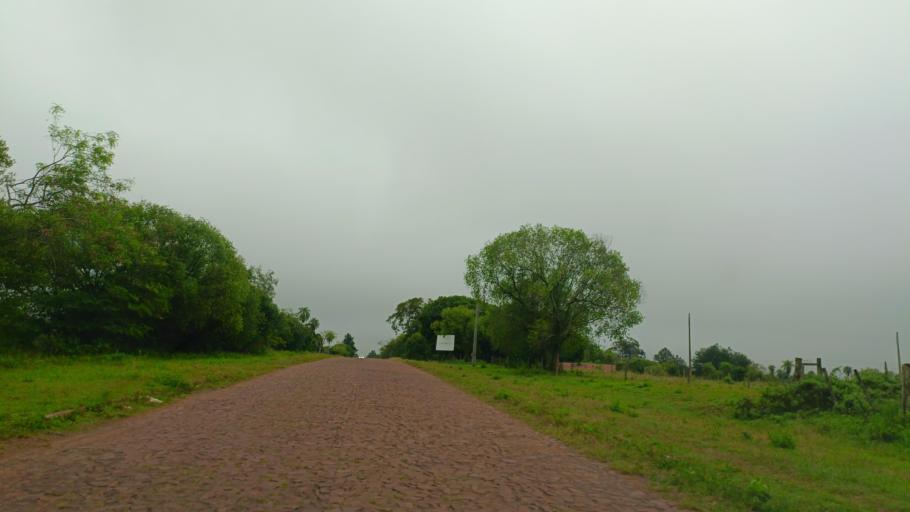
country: PY
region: Misiones
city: Santa Maria
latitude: -26.8776
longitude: -57.0128
